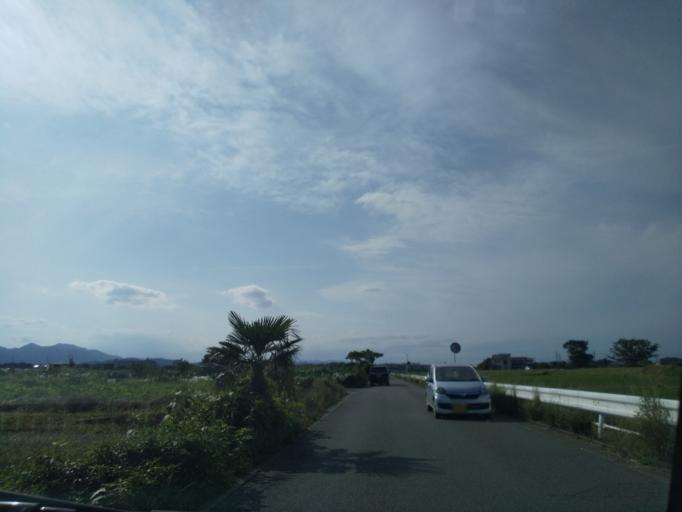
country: JP
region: Kanagawa
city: Zama
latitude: 35.4707
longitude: 139.3843
